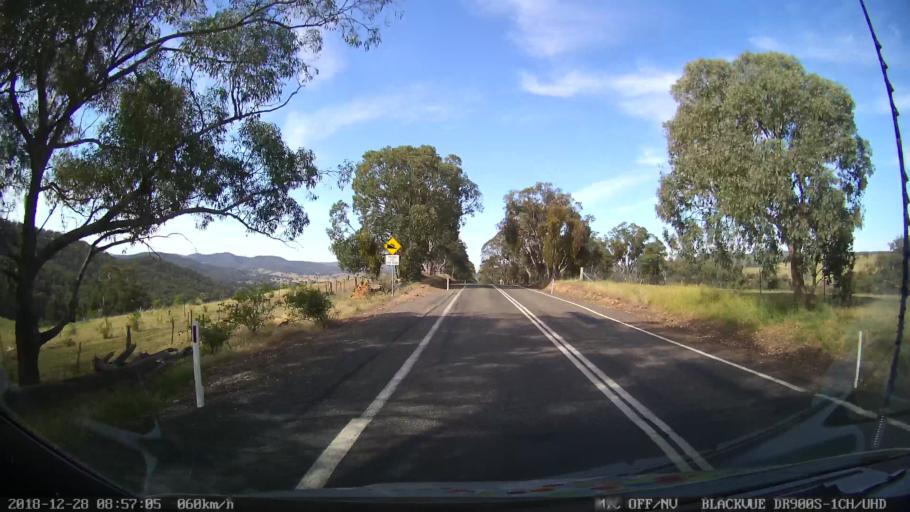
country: AU
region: New South Wales
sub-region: Upper Lachlan Shire
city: Crookwell
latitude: -34.1162
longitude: 149.3377
